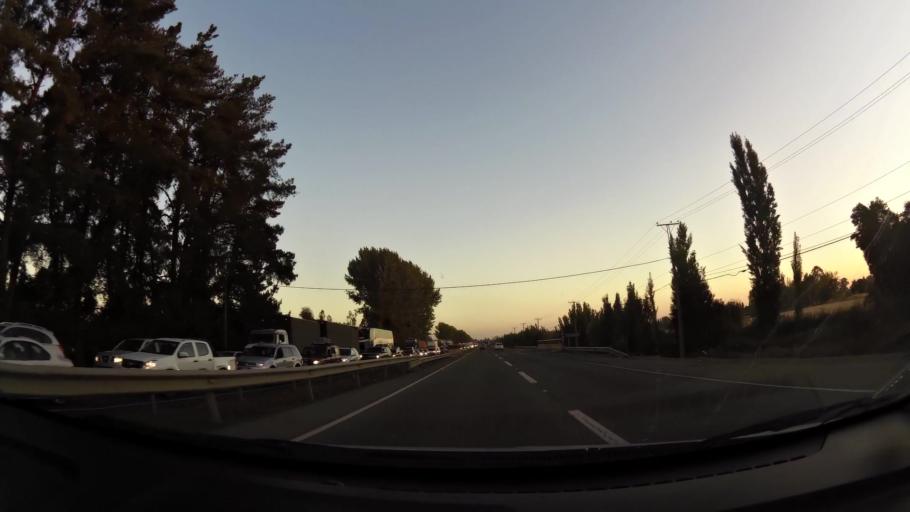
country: CL
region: Maule
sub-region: Provincia de Linares
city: Linares
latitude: -35.7532
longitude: -71.6729
